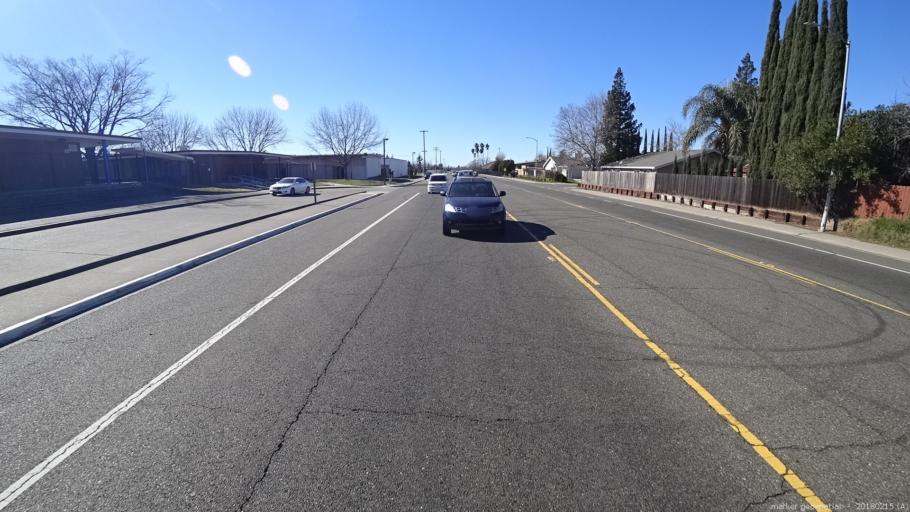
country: US
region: California
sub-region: Sacramento County
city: Foothill Farms
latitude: 38.6890
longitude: -121.3590
